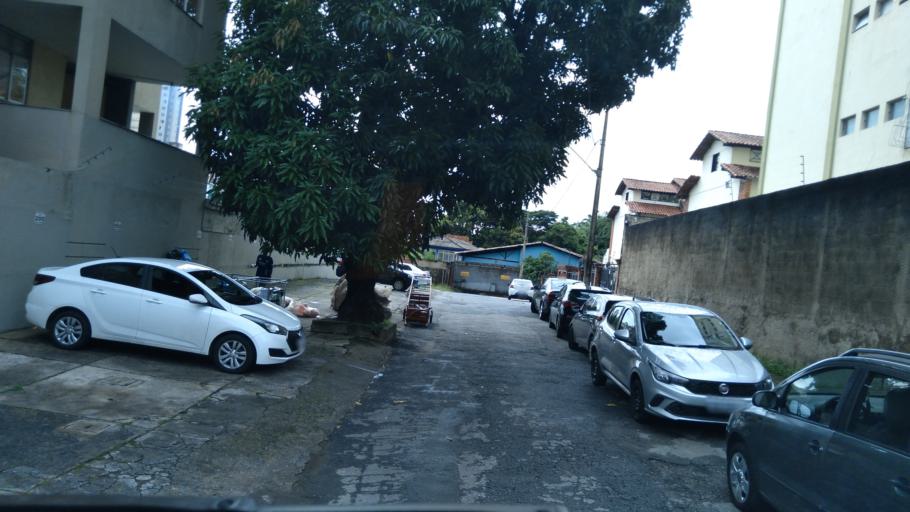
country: BR
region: Minas Gerais
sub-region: Contagem
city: Contagem
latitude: -19.9268
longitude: -43.9974
